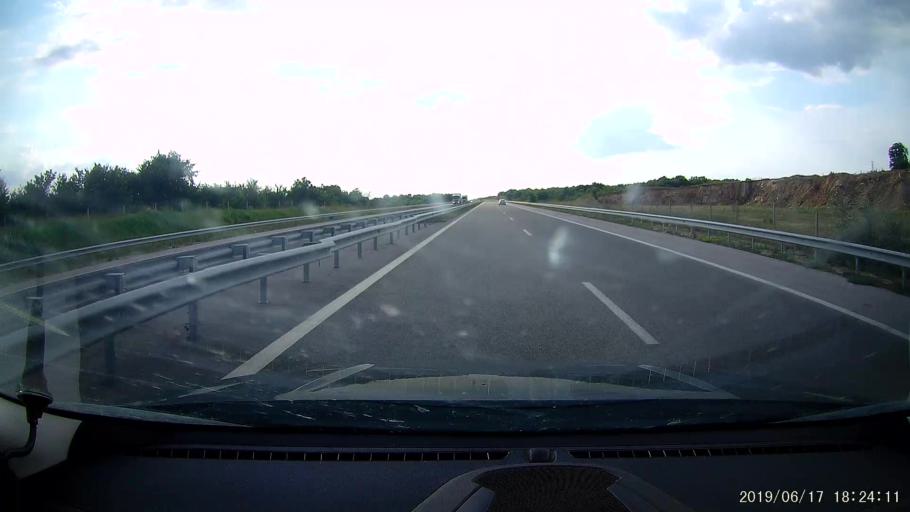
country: BG
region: Khaskovo
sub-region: Obshtina Dimitrovgrad
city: Dimitrovgrad
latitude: 41.9816
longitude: 25.6992
